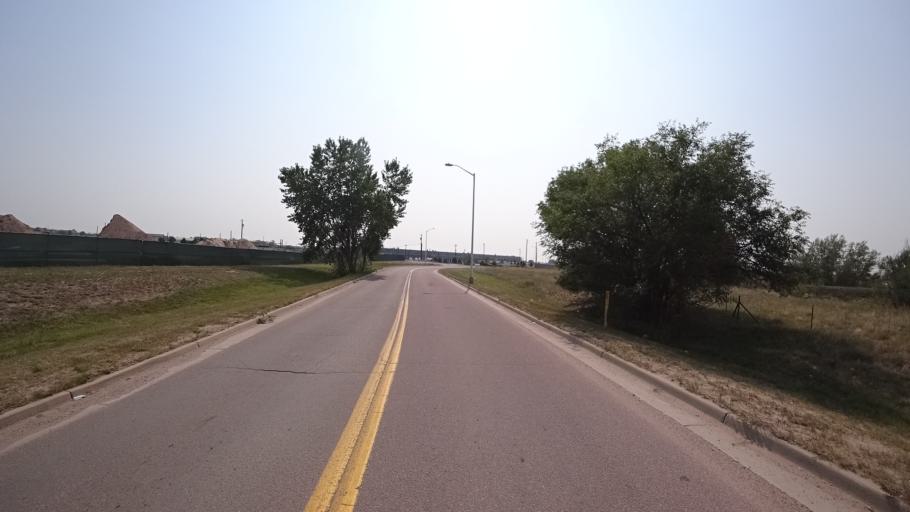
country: US
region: Colorado
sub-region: El Paso County
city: Cimarron Hills
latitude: 38.8366
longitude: -104.7254
